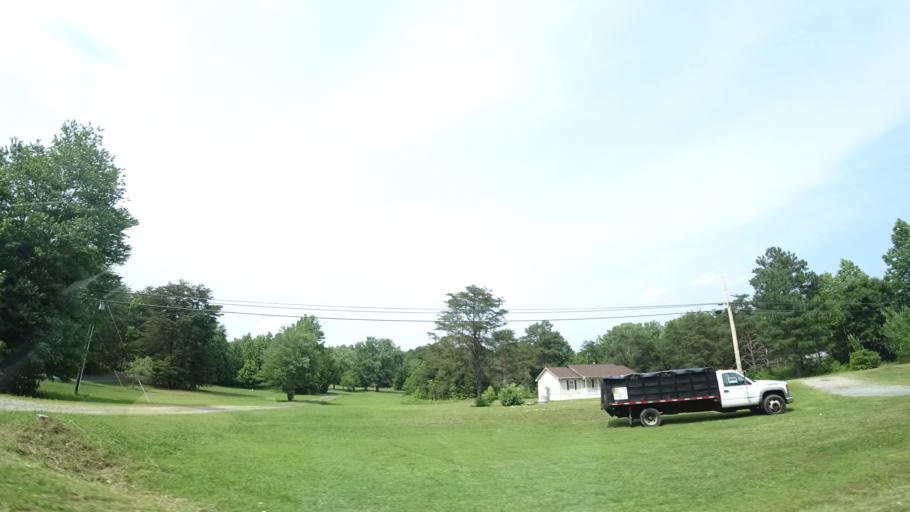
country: US
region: Virginia
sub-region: Spotsylvania County
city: Spotsylvania Courthouse
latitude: 38.1406
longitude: -77.5645
